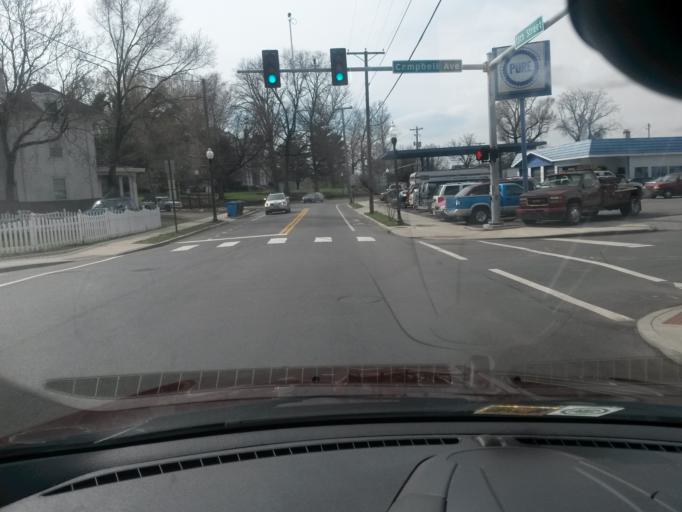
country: US
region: Virginia
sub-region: City of Roanoke
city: Roanoke
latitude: 37.2707
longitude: -79.9638
